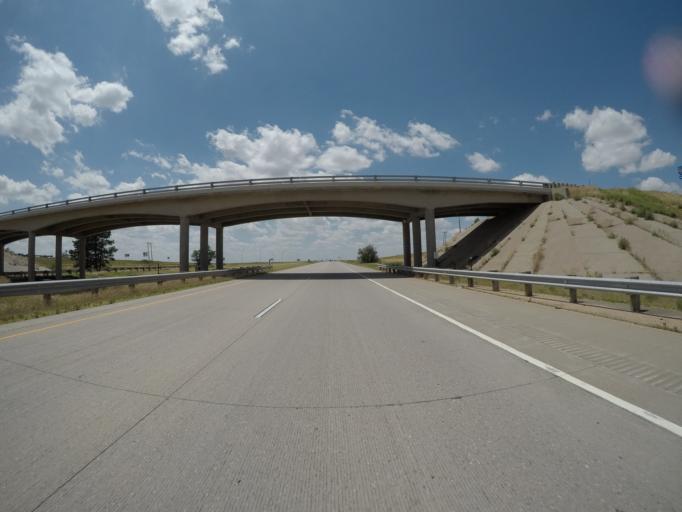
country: US
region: Colorado
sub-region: Kit Carson County
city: Burlington
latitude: 39.2943
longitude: -102.2784
